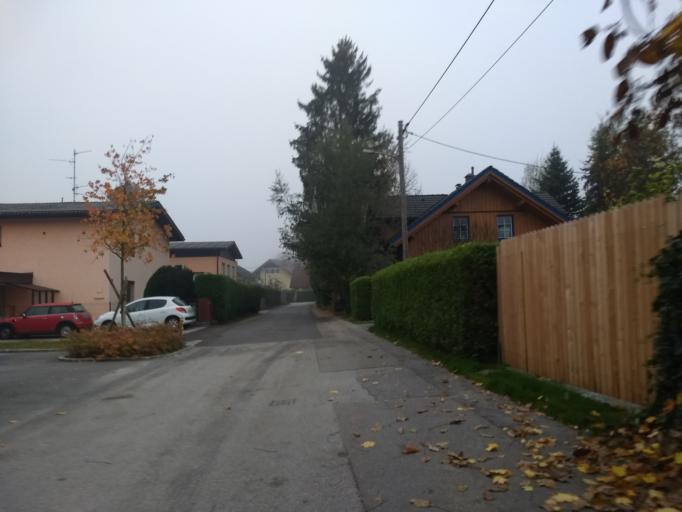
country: AT
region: Salzburg
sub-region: Salzburg Stadt
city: Salzburg
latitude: 47.7781
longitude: 13.0420
